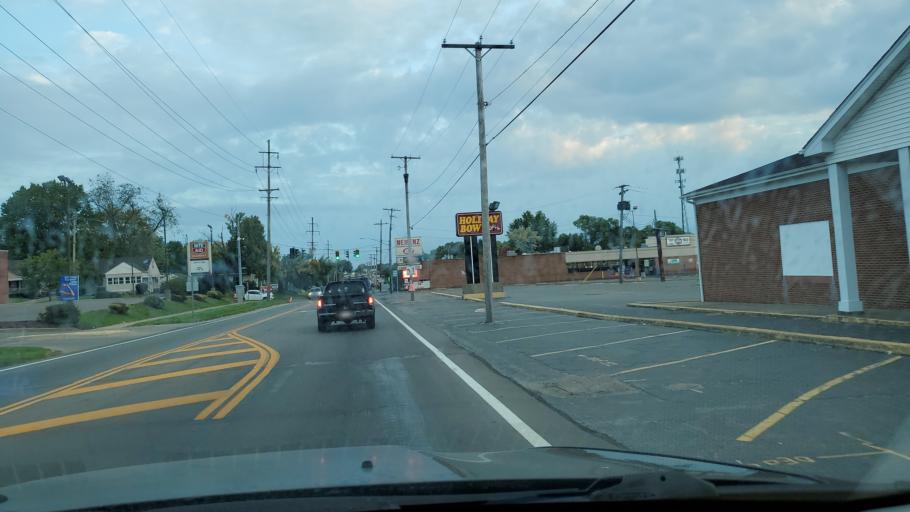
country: US
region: Ohio
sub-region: Mahoning County
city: Struthers
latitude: 41.0500
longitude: -80.6157
